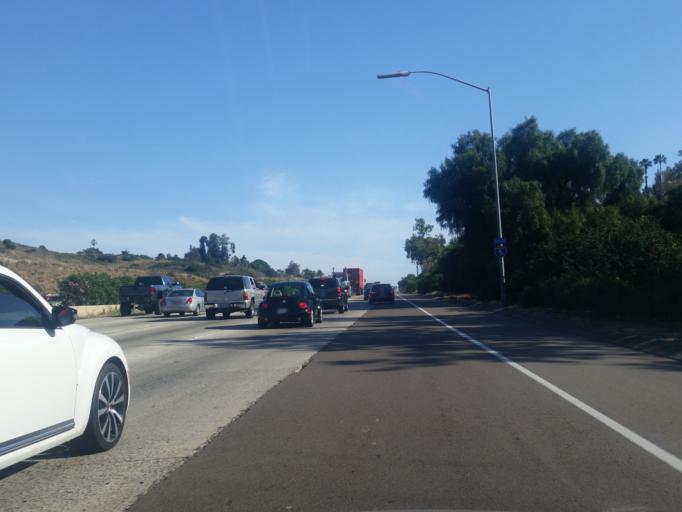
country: US
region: California
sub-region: San Diego County
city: Encinitas
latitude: 33.0804
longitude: -117.2971
